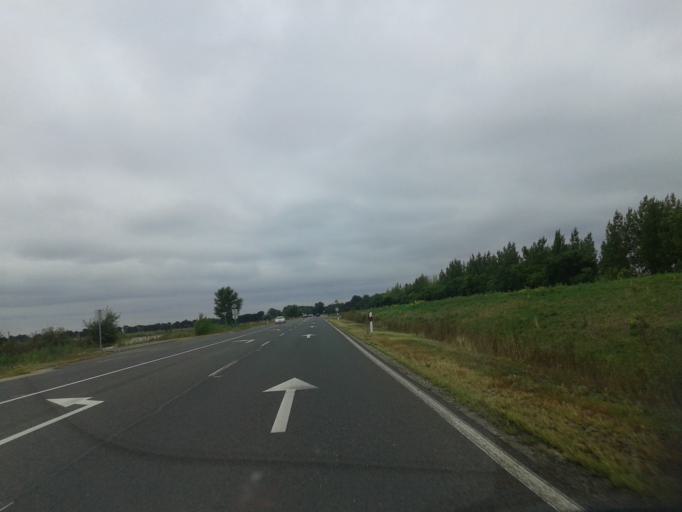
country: HU
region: Bacs-Kiskun
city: Harta
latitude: 46.7308
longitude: 19.0158
